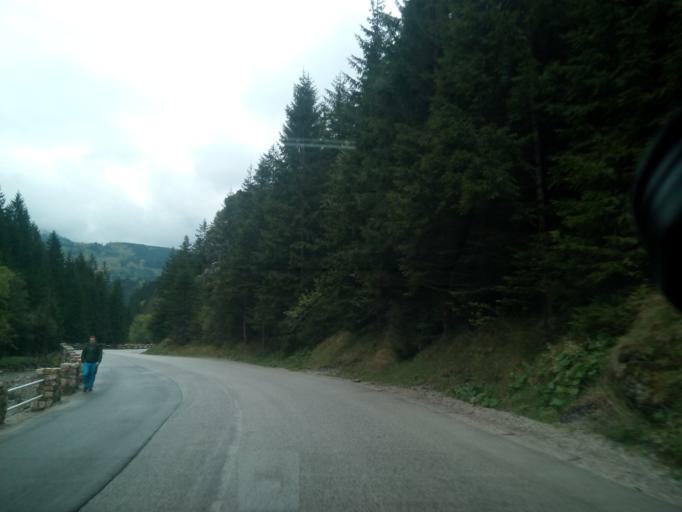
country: SK
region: Zilinsky
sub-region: Okres Zilina
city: Terchova
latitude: 49.2443
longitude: 19.0382
